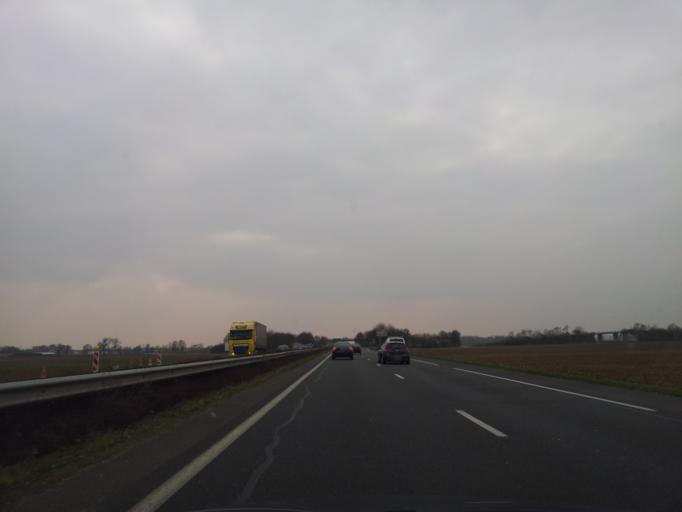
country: FR
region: Alsace
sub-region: Departement du Bas-Rhin
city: Lipsheim
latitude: 48.4820
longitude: 7.6719
